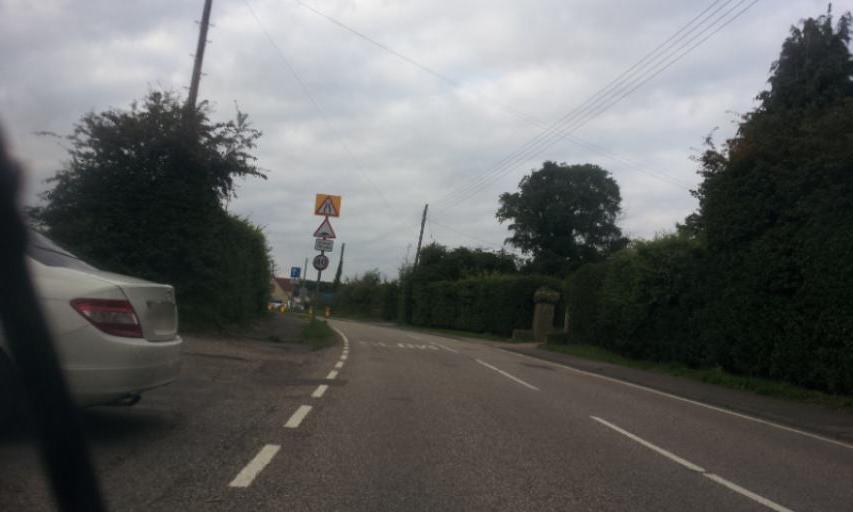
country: GB
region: England
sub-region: Kent
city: East Peckham
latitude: 51.2197
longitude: 0.3941
